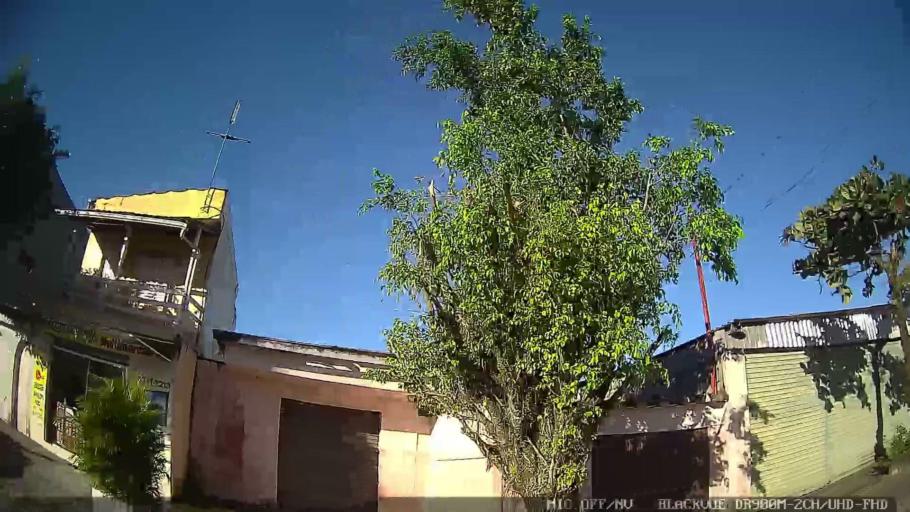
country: BR
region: Sao Paulo
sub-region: Santos
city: Santos
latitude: -23.9473
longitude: -46.2984
